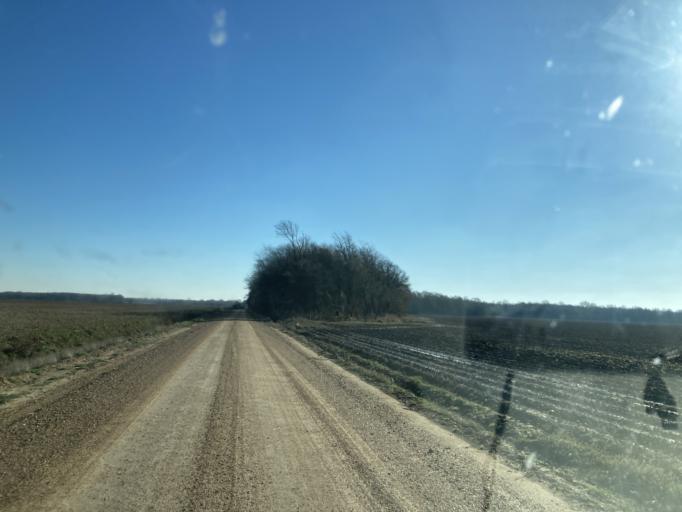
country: US
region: Mississippi
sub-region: Yazoo County
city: Yazoo City
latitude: 32.9373
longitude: -90.5850
